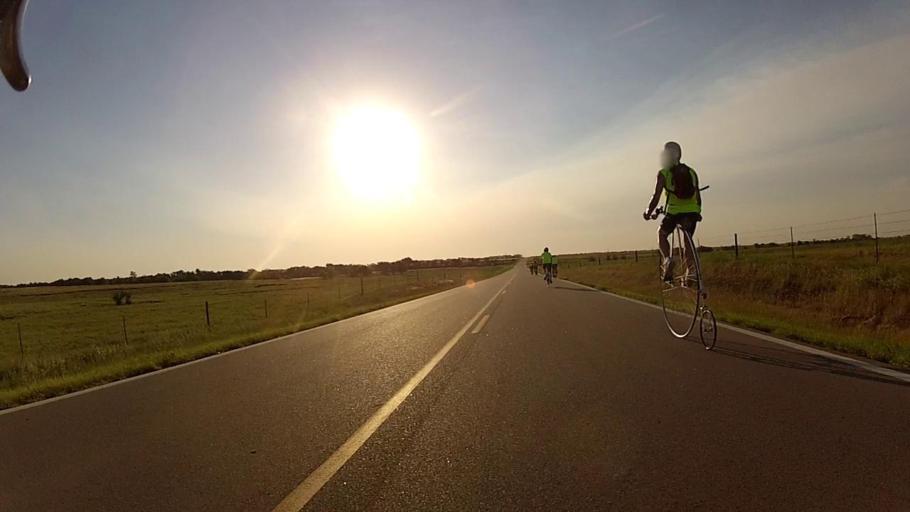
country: US
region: Kansas
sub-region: Harper County
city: Anthony
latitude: 37.1546
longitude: -97.8065
